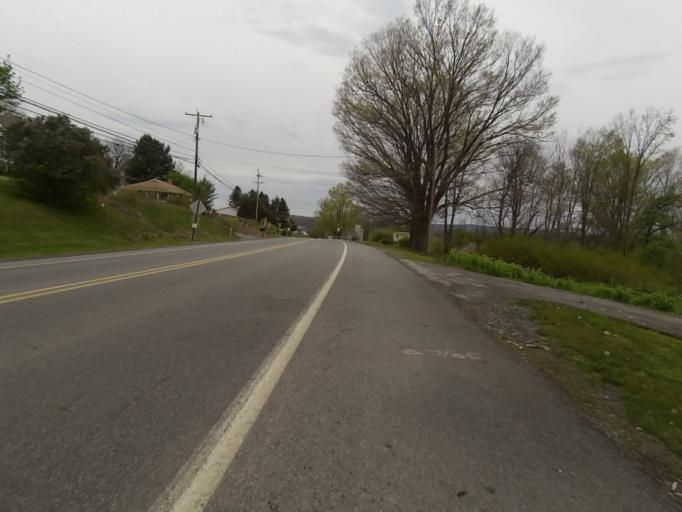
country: US
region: Pennsylvania
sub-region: Clearfield County
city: Troy
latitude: 40.9046
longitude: -78.2040
